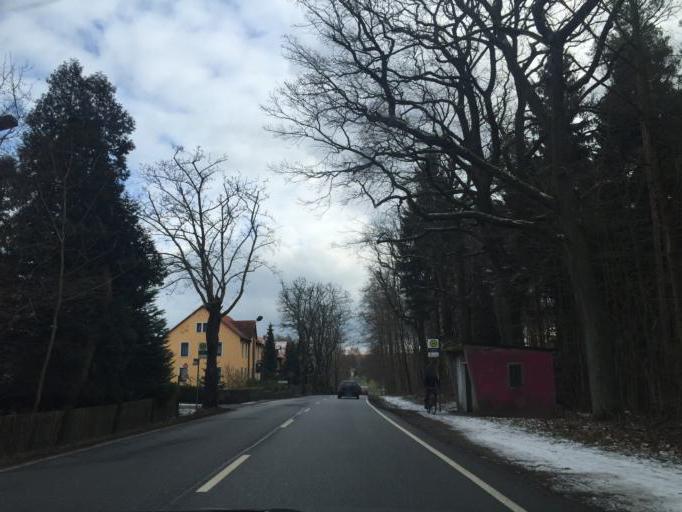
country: DE
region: Saxony
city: Radeberg
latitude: 51.1134
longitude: 13.8905
